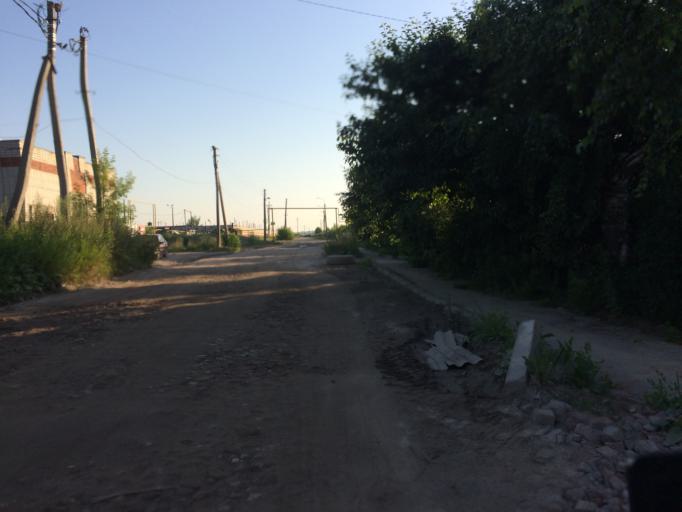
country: RU
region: Mariy-El
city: Yoshkar-Ola
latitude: 56.6546
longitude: 47.8869
